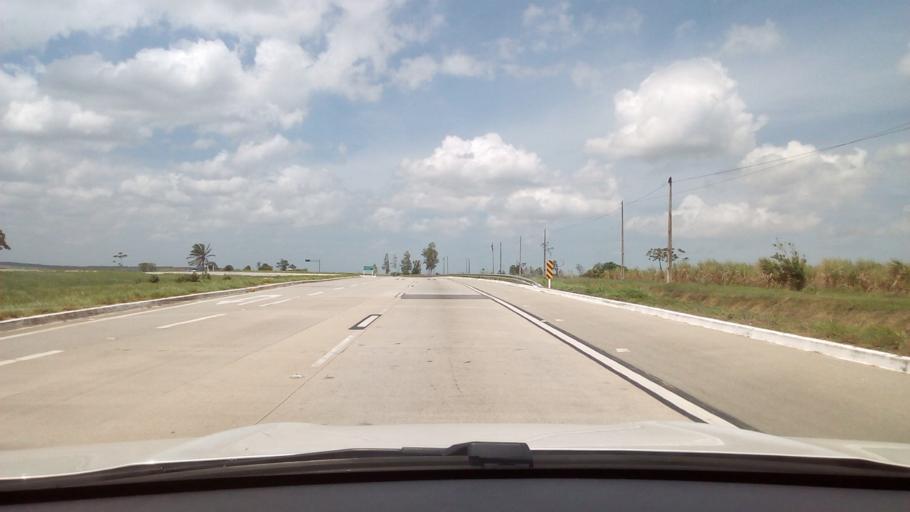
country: BR
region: Paraiba
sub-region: Mamanguape
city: Mamanguape
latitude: -6.7894
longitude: -35.1351
